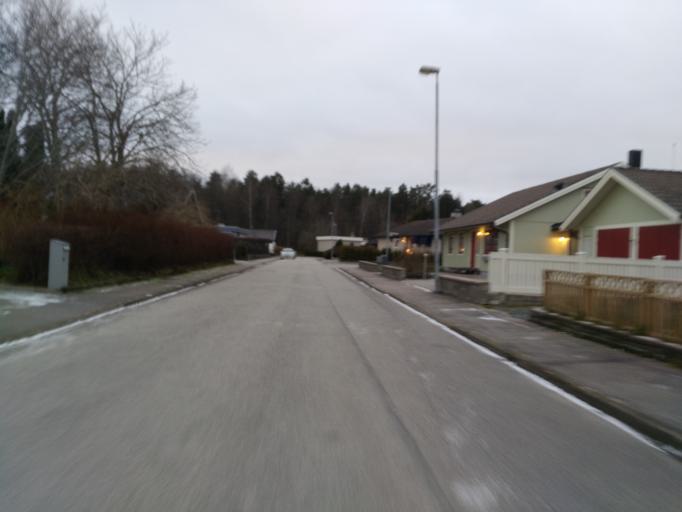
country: SE
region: Vaestra Goetaland
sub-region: Lidkopings Kommun
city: Lidkoping
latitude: 58.4903
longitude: 13.1676
